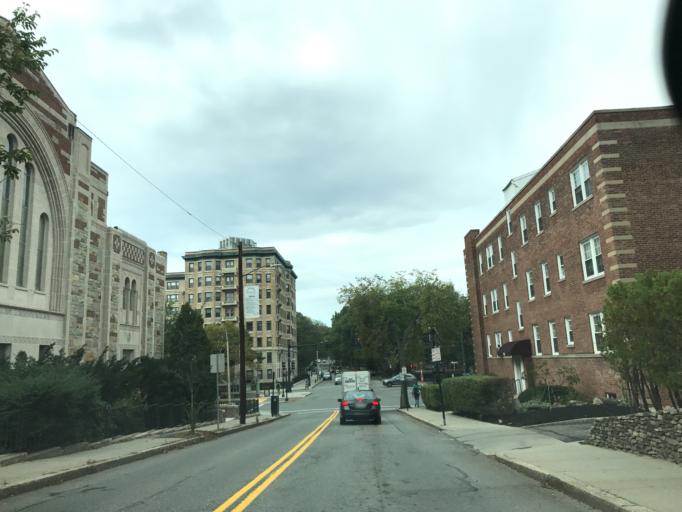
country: US
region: Massachusetts
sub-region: Norfolk County
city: Brookline
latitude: 42.3434
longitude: -71.1140
